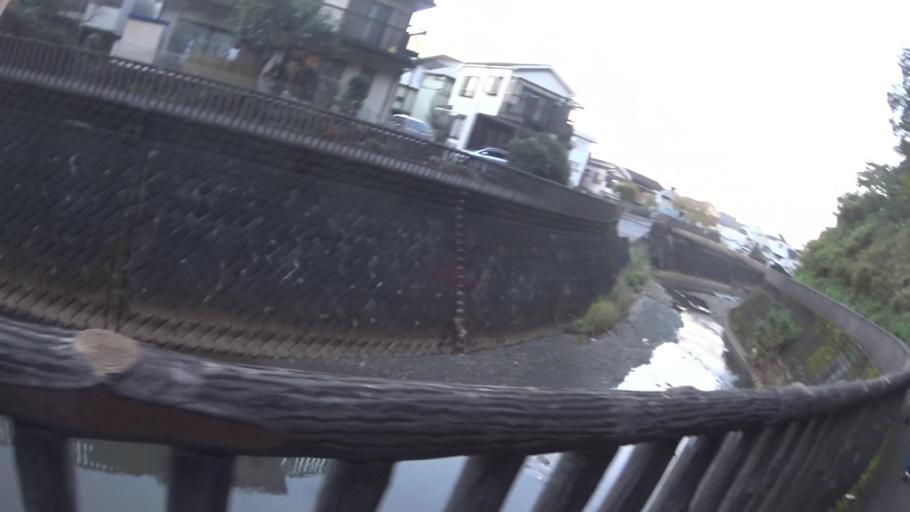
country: JP
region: Tokyo
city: Chofugaoka
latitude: 35.6329
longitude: 139.5241
